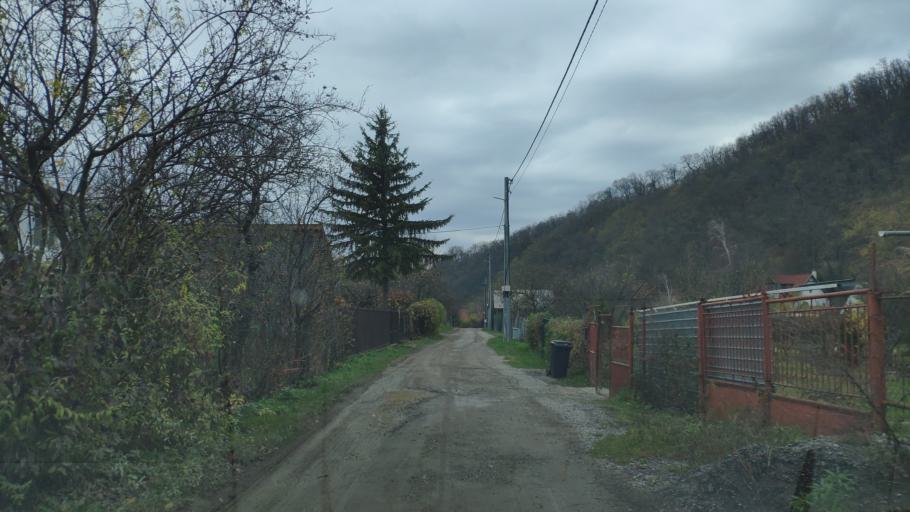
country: SK
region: Kosicky
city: Kosice
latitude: 48.6982
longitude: 21.2902
